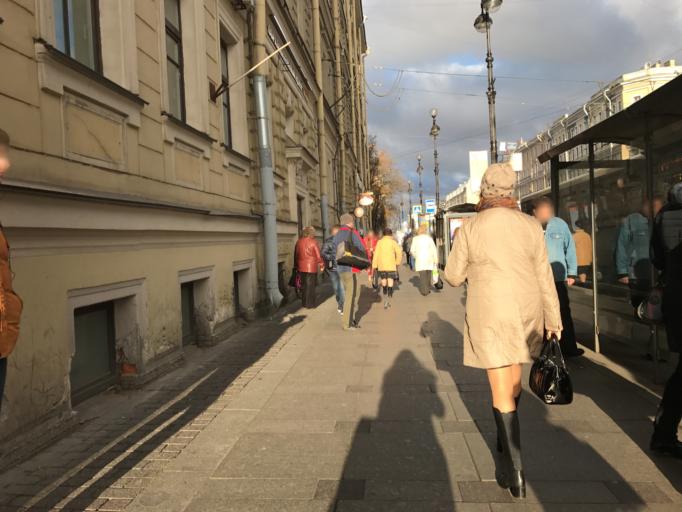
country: RU
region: St.-Petersburg
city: Centralniy
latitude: 59.9241
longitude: 30.3834
